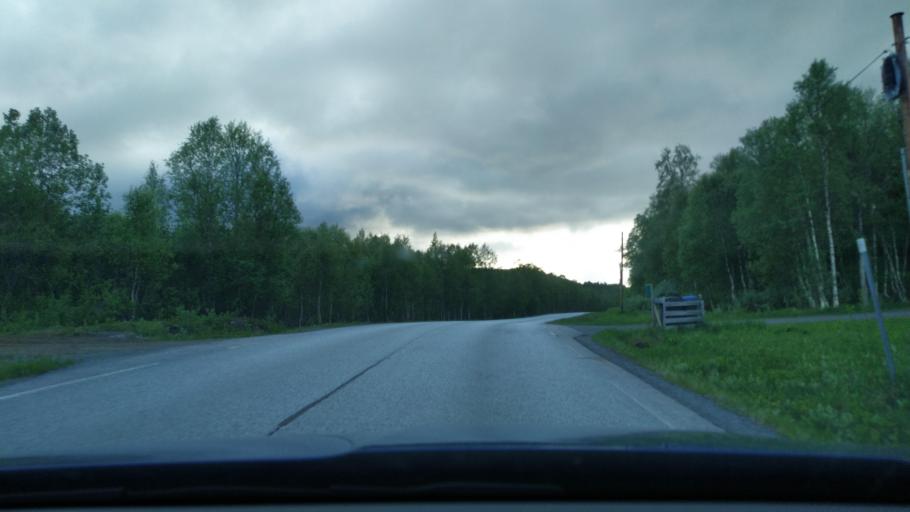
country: NO
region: Troms
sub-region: Dyroy
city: Brostadbotn
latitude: 69.0552
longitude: 17.7923
